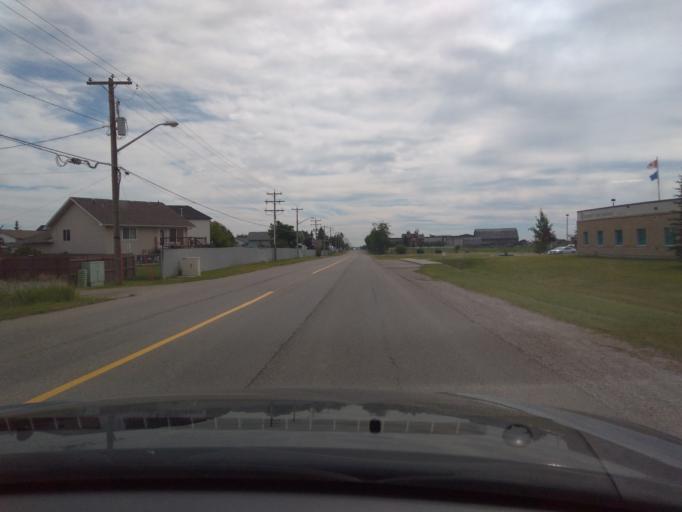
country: CA
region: Alberta
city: Didsbury
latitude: 51.6567
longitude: -114.1310
